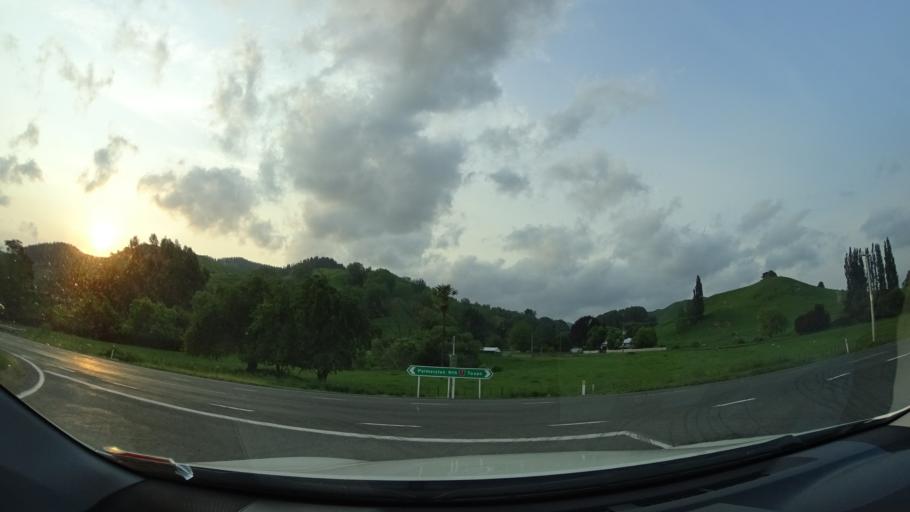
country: NZ
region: Manawatu-Wanganui
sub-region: Ruapehu District
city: Waiouru
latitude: -39.7522
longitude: 175.8339
